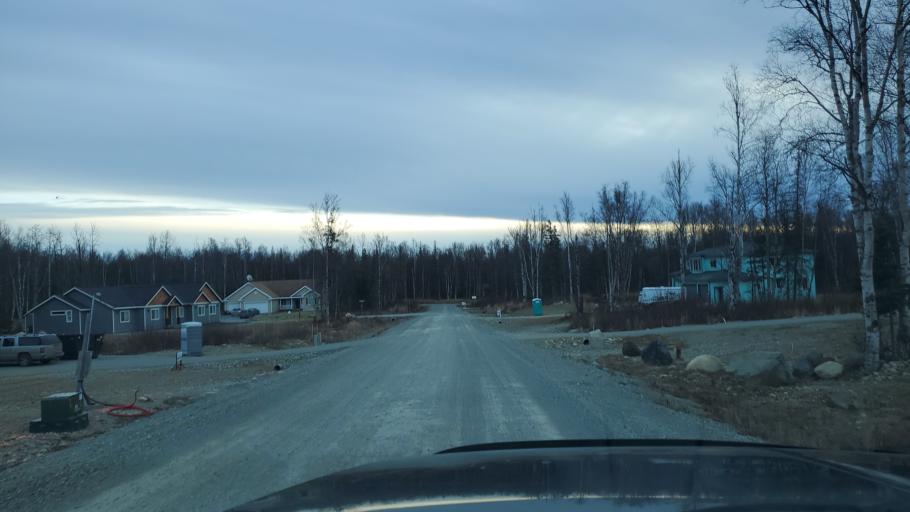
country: US
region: Alaska
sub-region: Matanuska-Susitna Borough
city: Lakes
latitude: 61.6554
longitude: -149.2911
